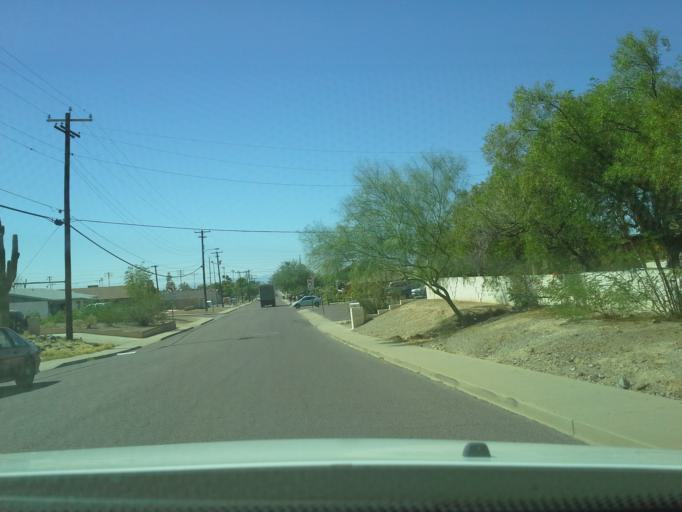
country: US
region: Arizona
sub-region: Maricopa County
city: Paradise Valley
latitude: 33.5678
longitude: -112.0536
